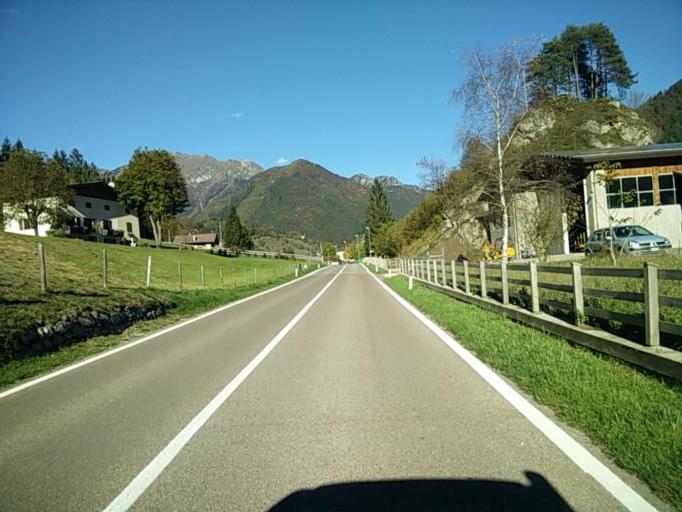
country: IT
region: Trentino-Alto Adige
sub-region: Provincia di Trento
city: Cimego
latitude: 45.8811
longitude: 10.6648
